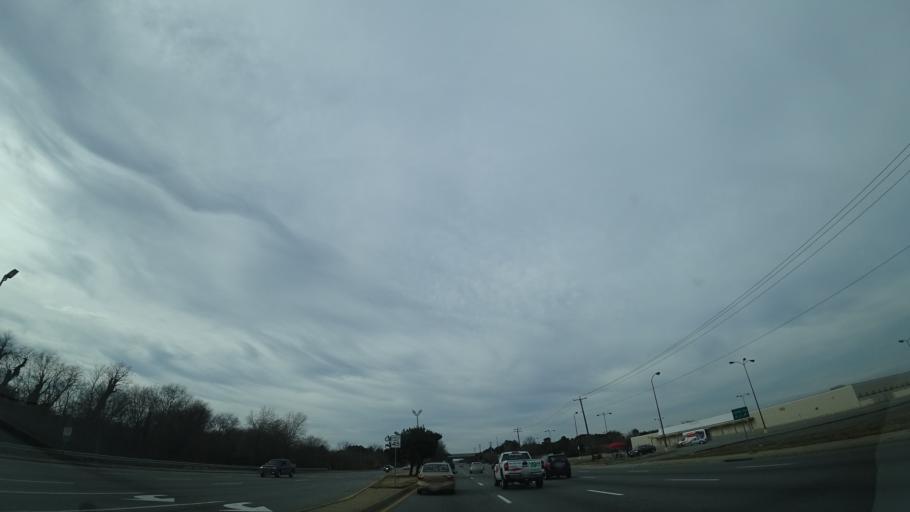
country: US
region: Virginia
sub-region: City of Hampton
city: Hampton
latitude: 37.0437
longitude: -76.3592
